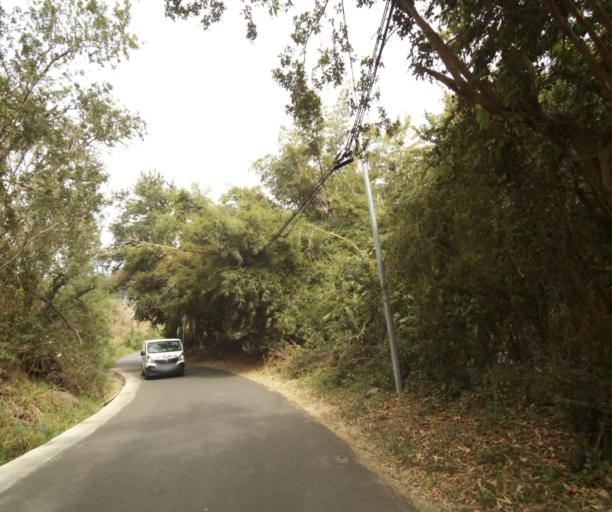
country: RE
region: Reunion
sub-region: Reunion
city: Saint-Paul
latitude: -20.9918
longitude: 55.3038
